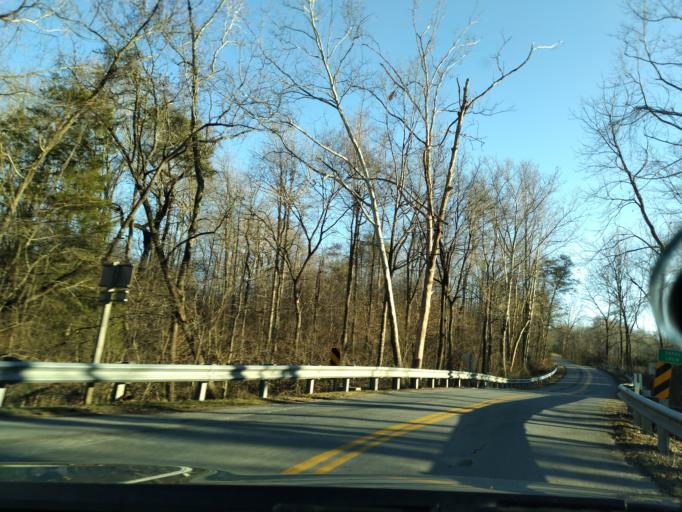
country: US
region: Virginia
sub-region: Prince Edward County
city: Hampden Sydney
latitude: 37.3123
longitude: -78.5658
